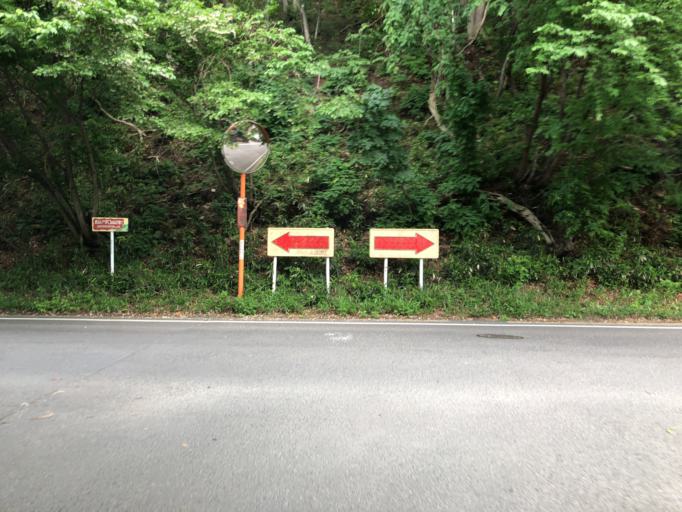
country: JP
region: Fukushima
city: Fukushima-shi
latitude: 37.7731
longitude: 140.4544
